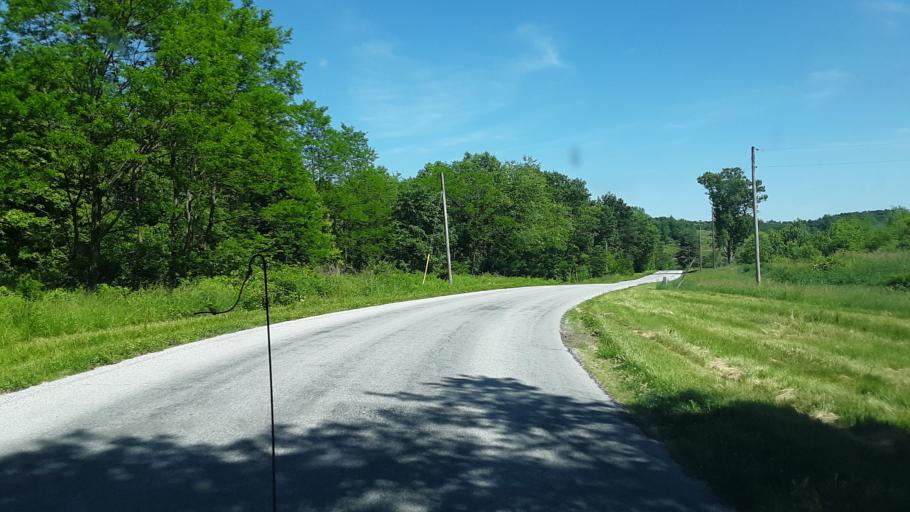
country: US
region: Ohio
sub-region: Coshocton County
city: Coshocton
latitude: 40.2302
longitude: -81.8300
